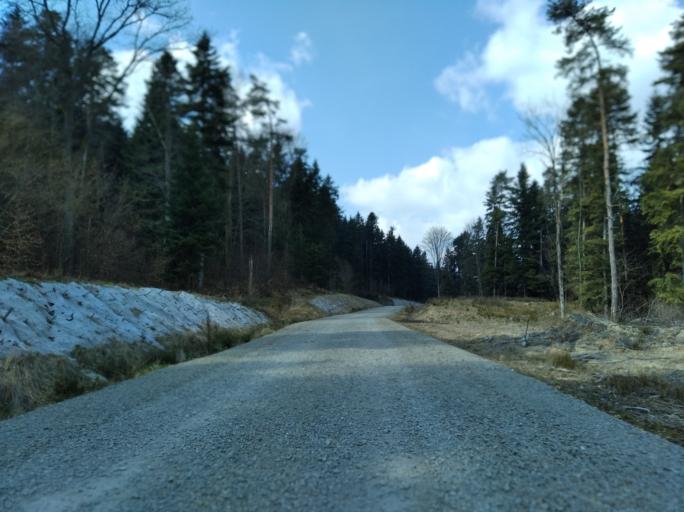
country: PL
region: Subcarpathian Voivodeship
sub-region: Powiat strzyzowski
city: Strzyzow
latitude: 49.8186
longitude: 21.8095
